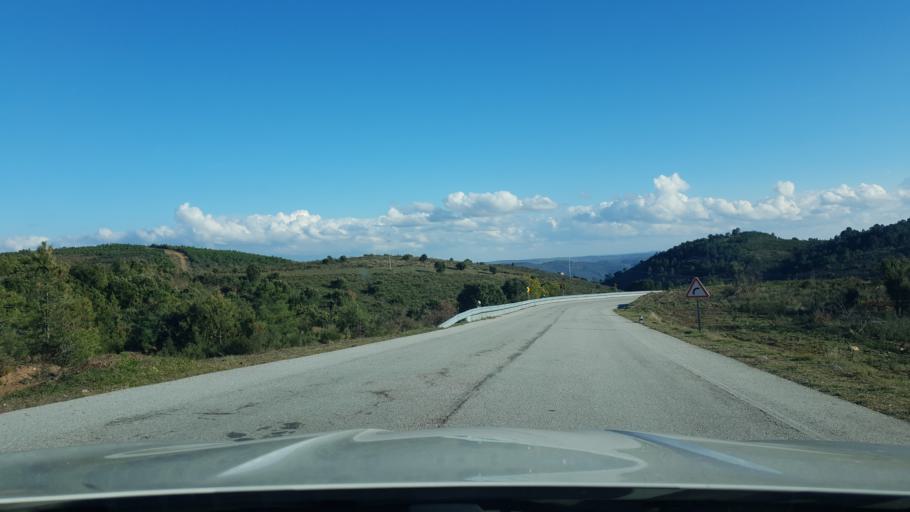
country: PT
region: Braganca
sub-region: Freixo de Espada A Cinta
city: Freixo de Espada a Cinta
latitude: 41.1277
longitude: -6.8161
